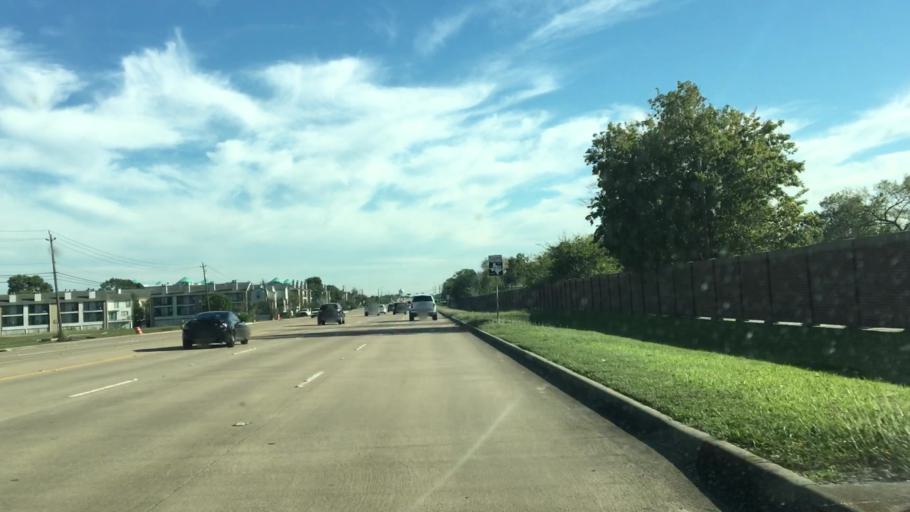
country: US
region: Texas
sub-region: Harris County
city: Nassau Bay
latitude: 29.5422
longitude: -95.1029
